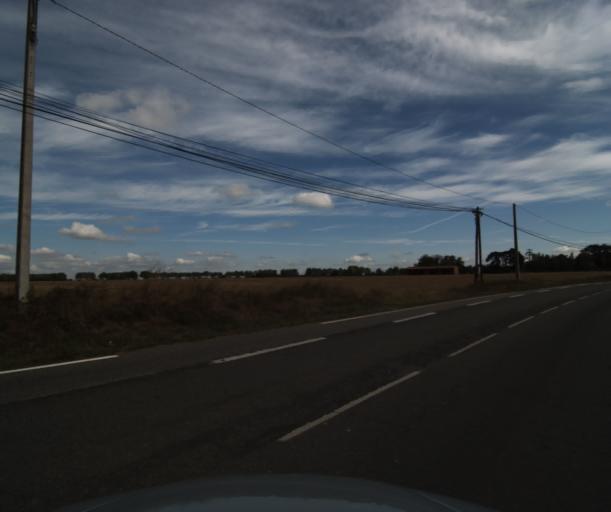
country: FR
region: Midi-Pyrenees
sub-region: Departement de la Haute-Garonne
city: Seysses
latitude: 43.4586
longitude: 1.2934
